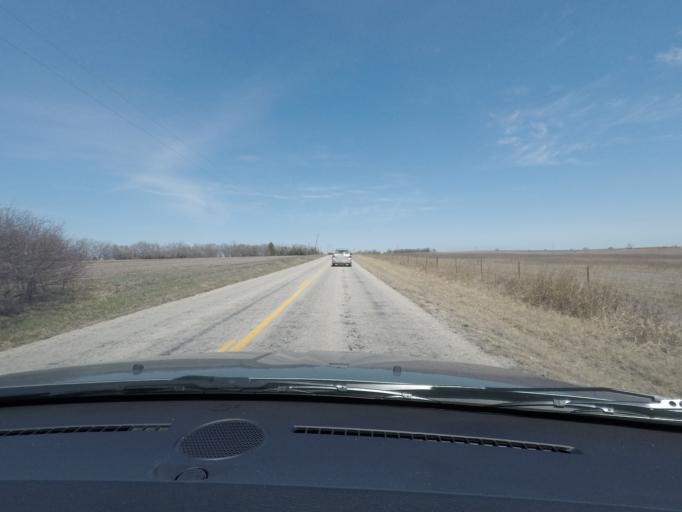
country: US
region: Kansas
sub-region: Lyon County
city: Emporia
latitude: 38.6047
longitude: -96.1696
